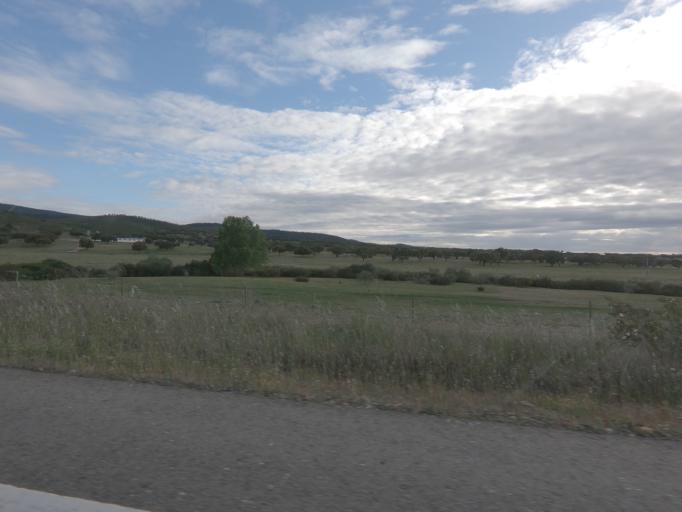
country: ES
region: Extremadura
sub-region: Provincia de Caceres
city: Pedroso de Acim
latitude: 39.8512
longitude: -6.4177
